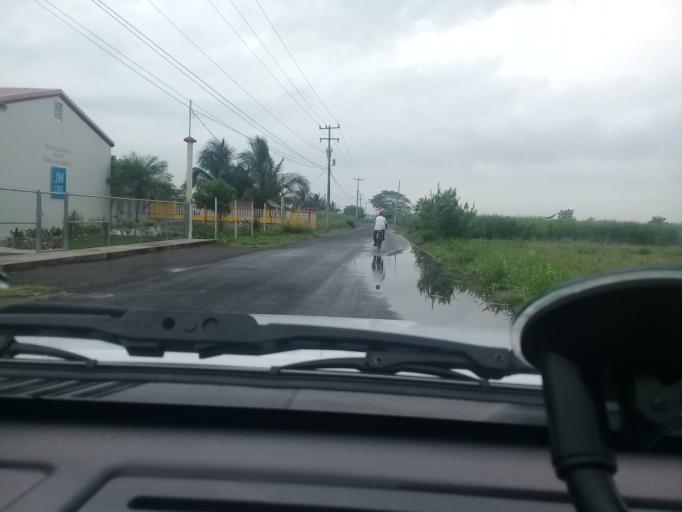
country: MX
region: Veracruz
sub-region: La Antigua
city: Nicolas Blanco (San Pancho)
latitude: 19.3526
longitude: -96.3455
